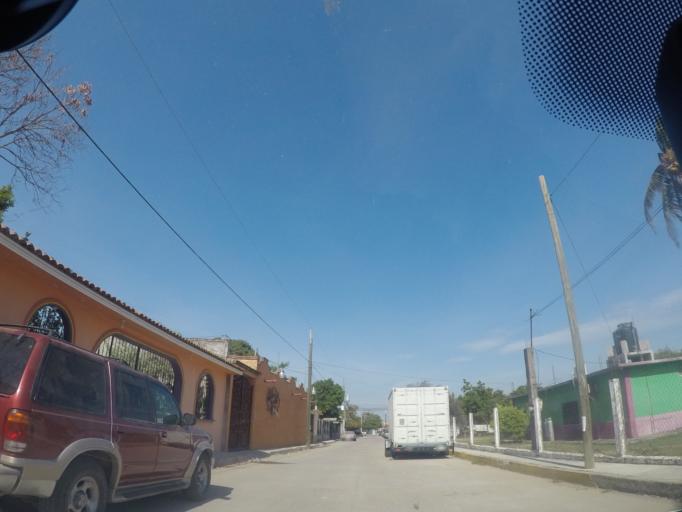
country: MX
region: Oaxaca
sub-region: Salina Cruz
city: Salina Cruz
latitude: 16.2157
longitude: -95.1980
